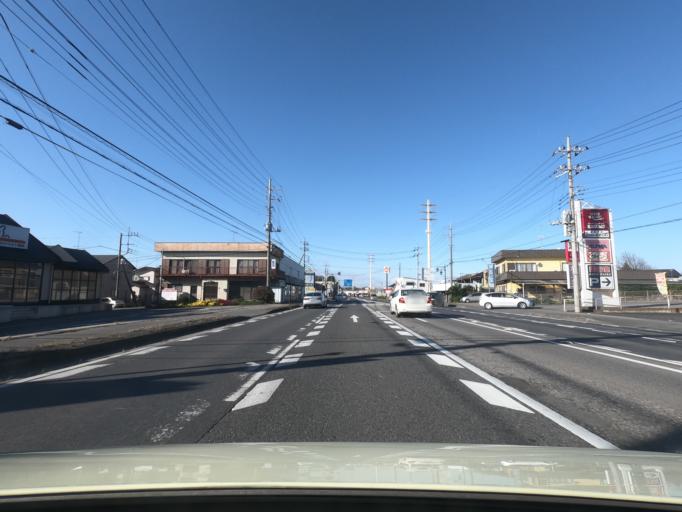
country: JP
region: Ibaraki
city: Ishige
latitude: 36.1815
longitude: 139.9512
